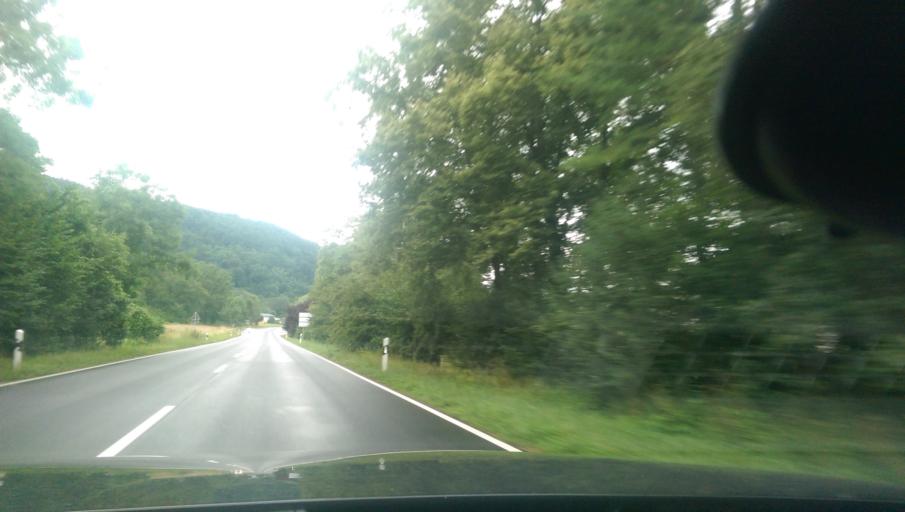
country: DE
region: Hesse
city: Witzenhausen
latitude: 51.3219
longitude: 9.8480
